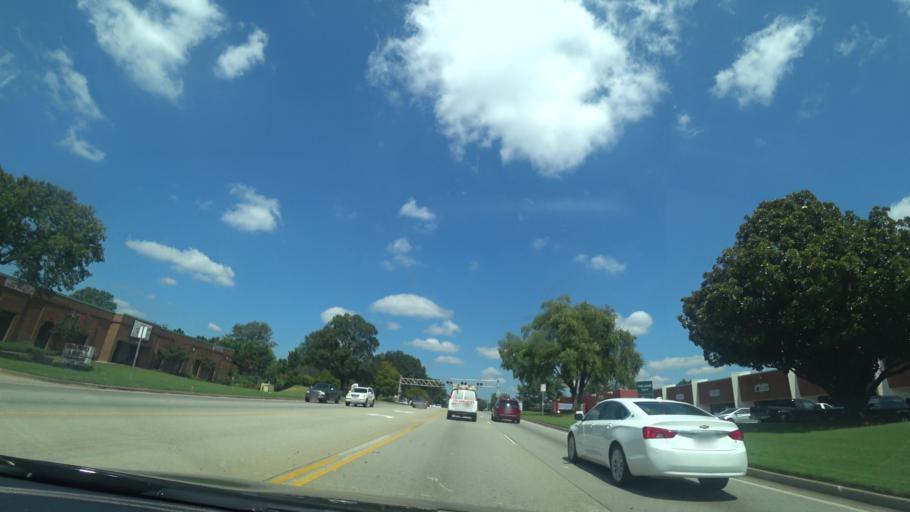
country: US
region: Georgia
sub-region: Gwinnett County
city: Norcross
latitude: 33.9379
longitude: -84.2355
